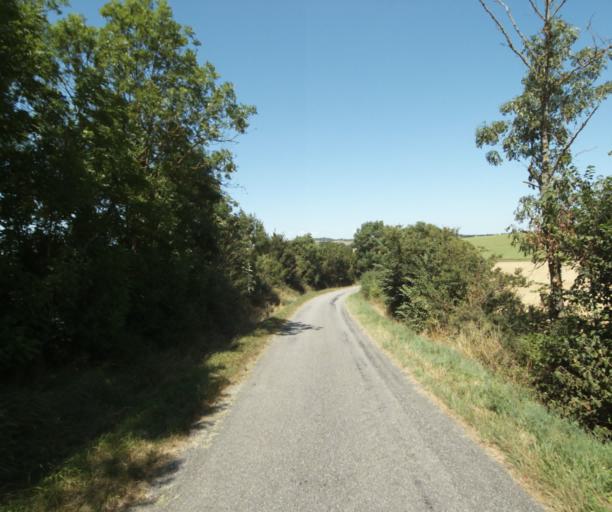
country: FR
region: Midi-Pyrenees
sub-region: Departement de la Haute-Garonne
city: Saint-Felix-Lauragais
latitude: 43.4621
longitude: 1.8919
